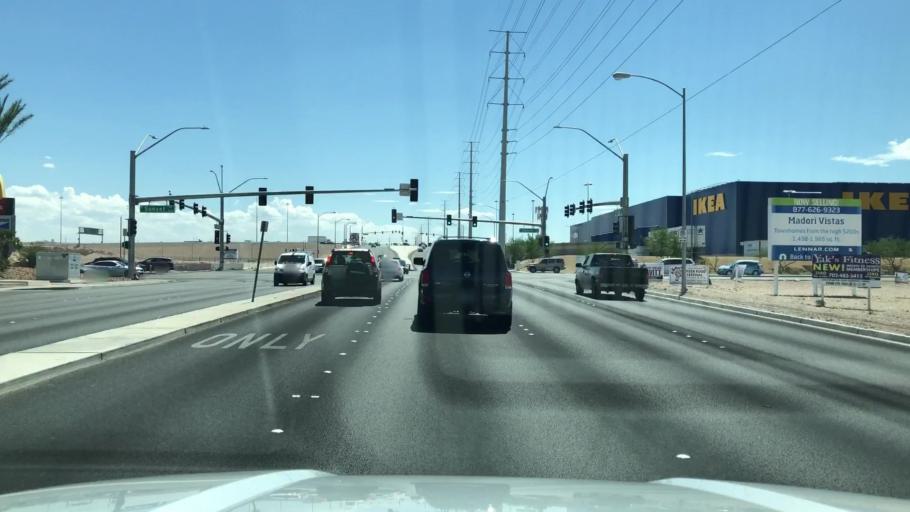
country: US
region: Nevada
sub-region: Clark County
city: Spring Valley
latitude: 36.0710
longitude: -115.2795
